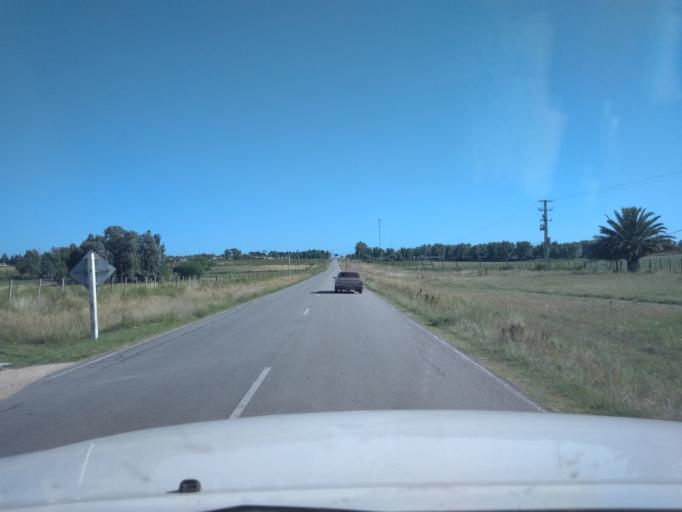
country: UY
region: Canelones
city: San Ramon
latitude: -34.3151
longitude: -55.9592
